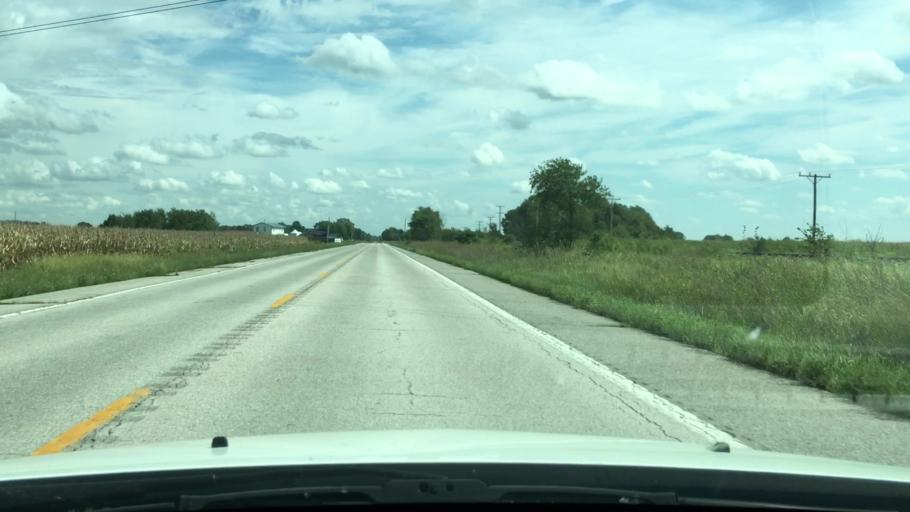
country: US
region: Missouri
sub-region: Audrain County
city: Vandalia
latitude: 39.2913
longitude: -91.5372
